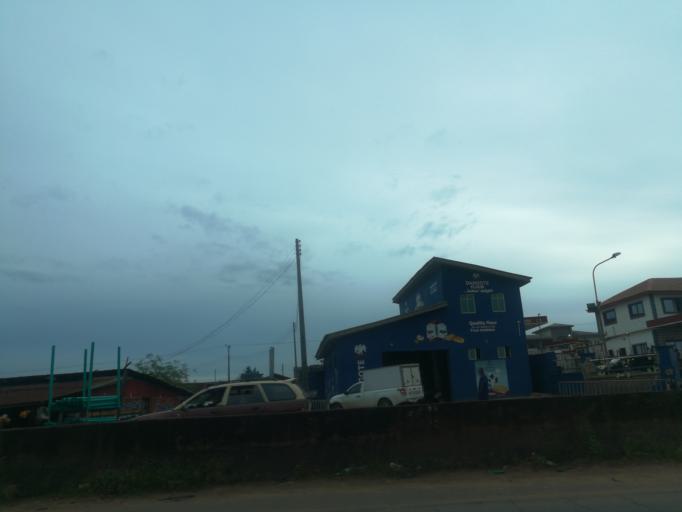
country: NG
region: Oyo
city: Egbeda
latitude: 7.3863
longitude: 3.9839
